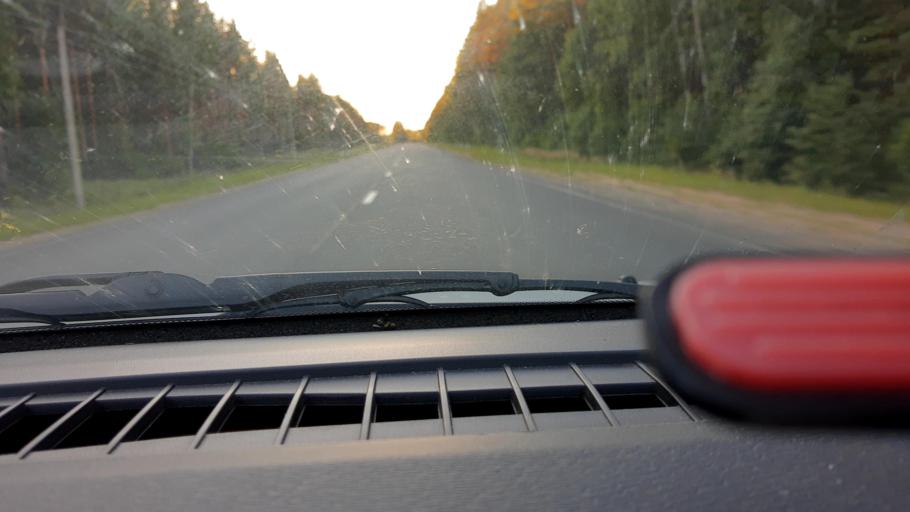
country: RU
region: Nizjnij Novgorod
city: Uren'
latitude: 57.3623
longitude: 45.6976
